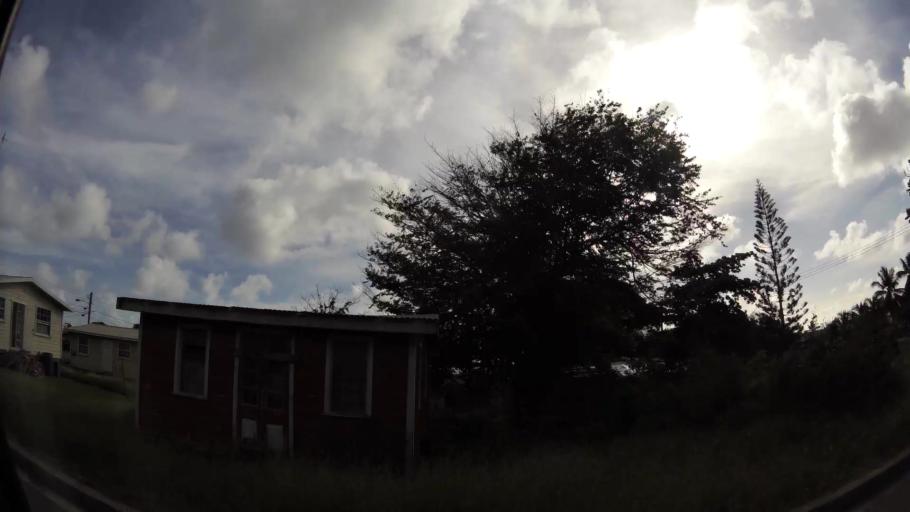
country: BB
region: Saint Michael
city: Bridgetown
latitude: 13.0859
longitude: -59.5821
